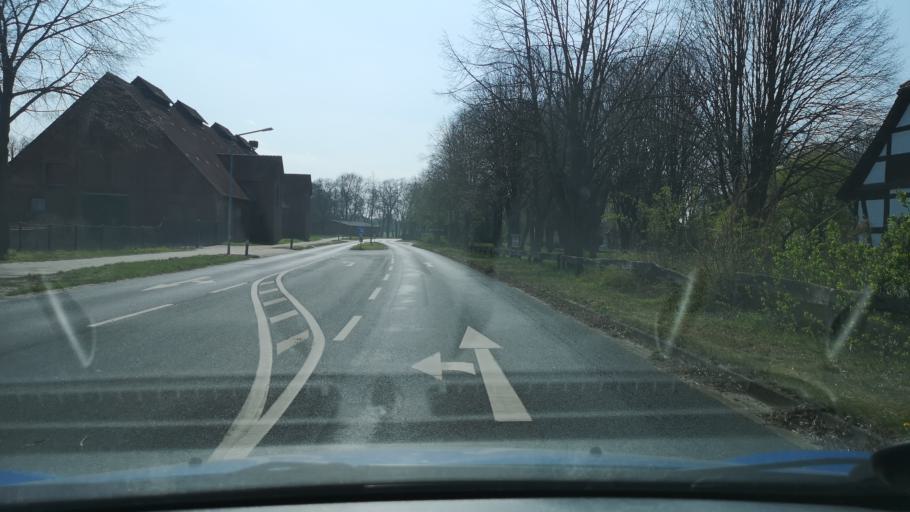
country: DE
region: Lower Saxony
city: Neustadt am Rubenberge
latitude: 52.5059
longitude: 9.5008
